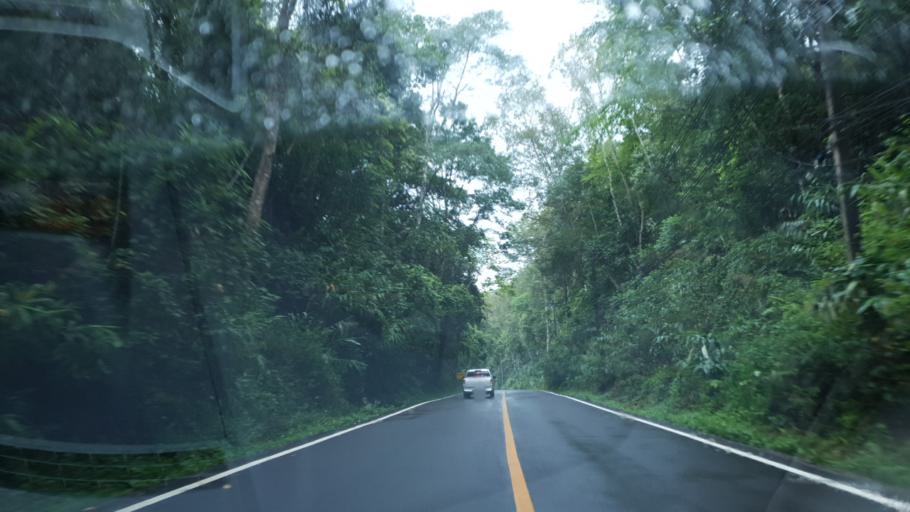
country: TH
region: Mae Hong Son
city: Ban Huai I Huak
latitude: 18.1429
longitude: 98.0891
